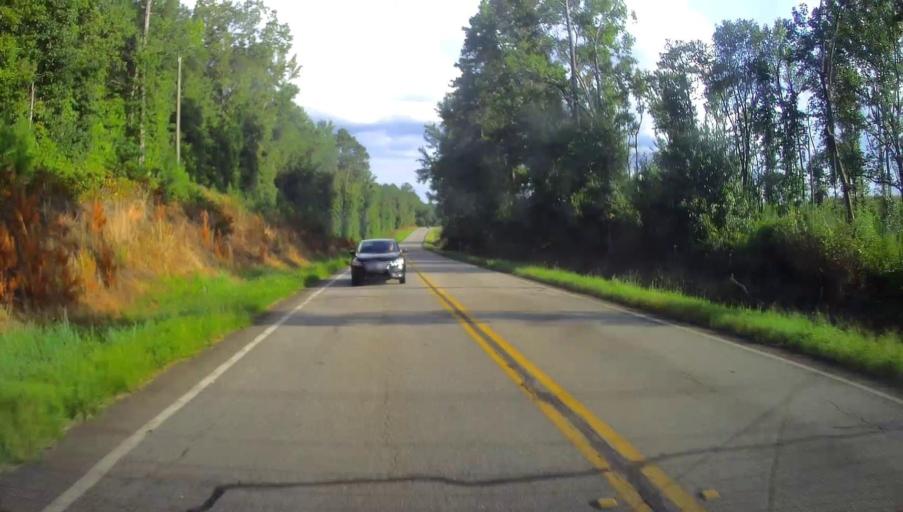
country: US
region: Georgia
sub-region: Crawford County
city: Knoxville
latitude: 32.8721
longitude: -83.9943
